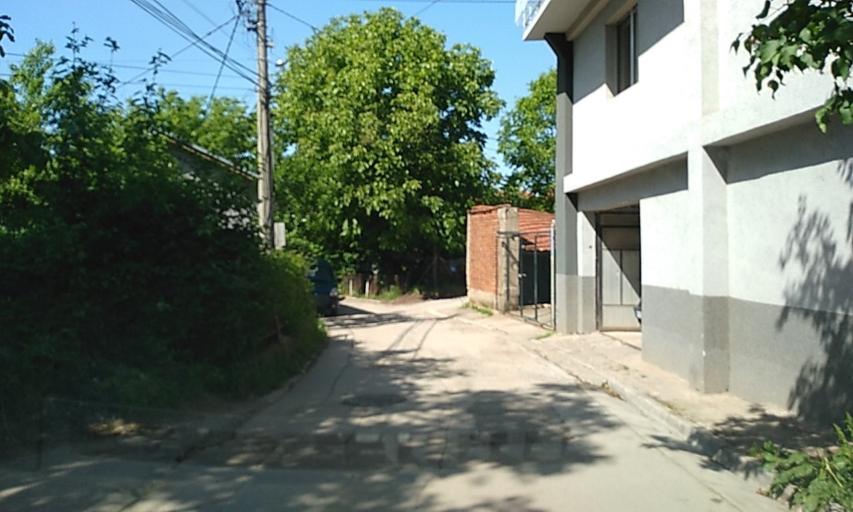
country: RS
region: Central Serbia
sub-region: Nisavski Okrug
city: Niska Banja
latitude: 43.2940
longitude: 22.0152
